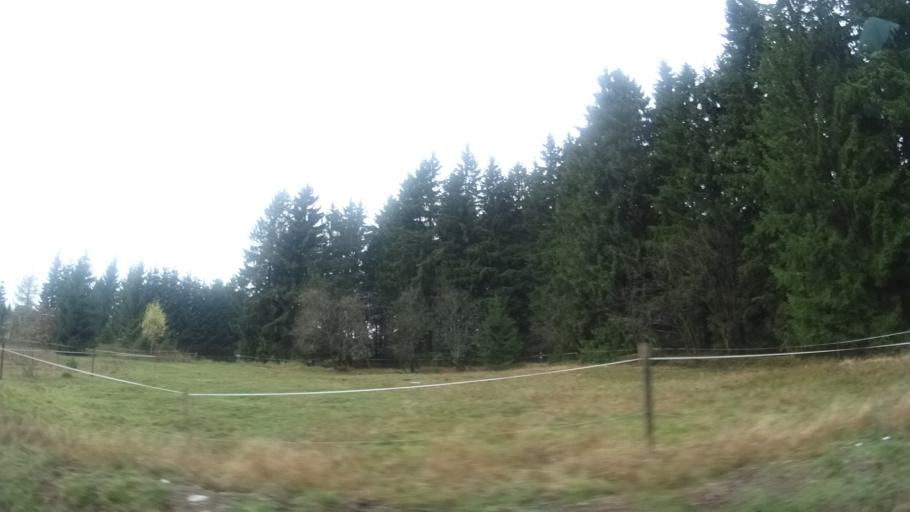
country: DE
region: Thuringia
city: Steinheid
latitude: 50.4756
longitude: 11.0856
